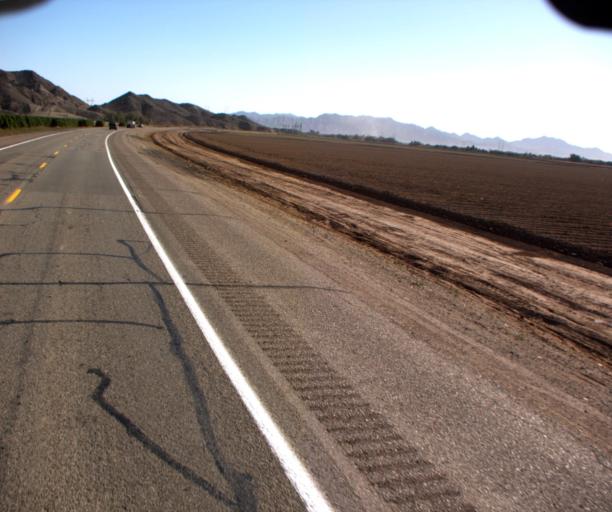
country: US
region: Arizona
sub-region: Yuma County
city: Fortuna Foothills
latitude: 32.7655
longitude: -114.4063
